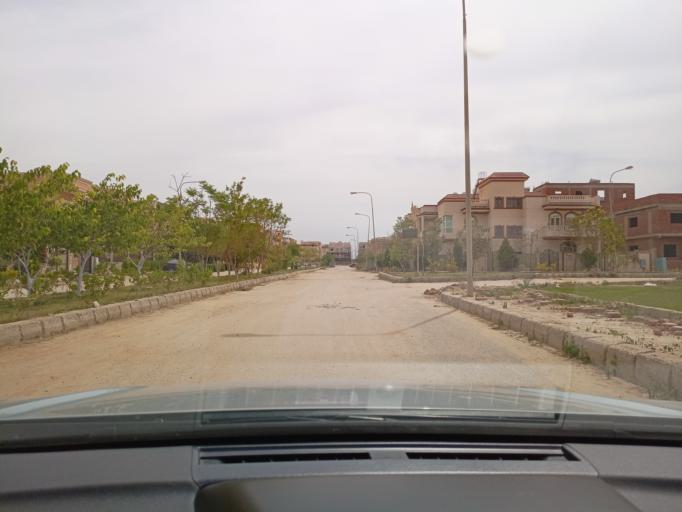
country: EG
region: Muhafazat al Qalyubiyah
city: Al Khankah
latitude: 30.2467
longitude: 31.5027
